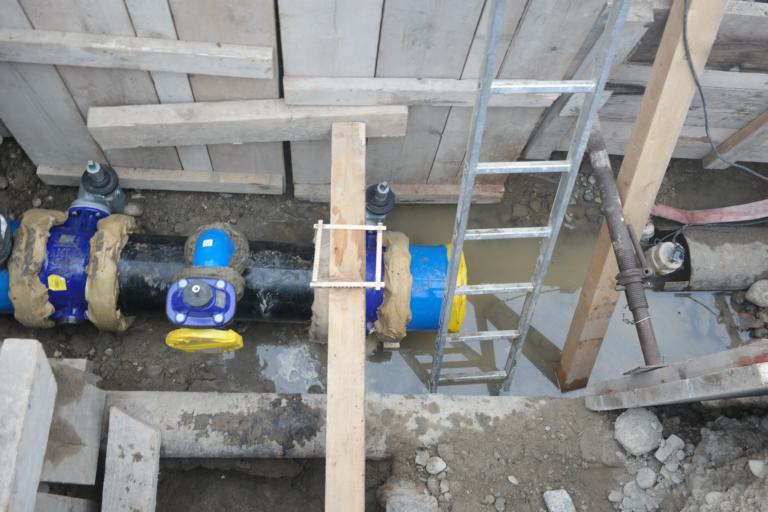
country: CH
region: Geneva
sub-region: Geneva
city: Les Avanchets
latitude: 46.2106
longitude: 6.1153
